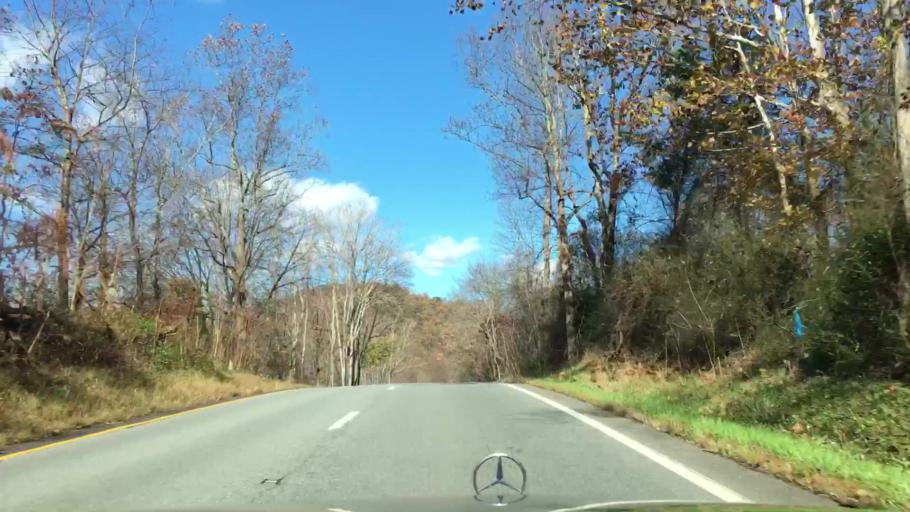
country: US
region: Virginia
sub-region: Nelson County
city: Nellysford
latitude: 37.8799
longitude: -78.7141
